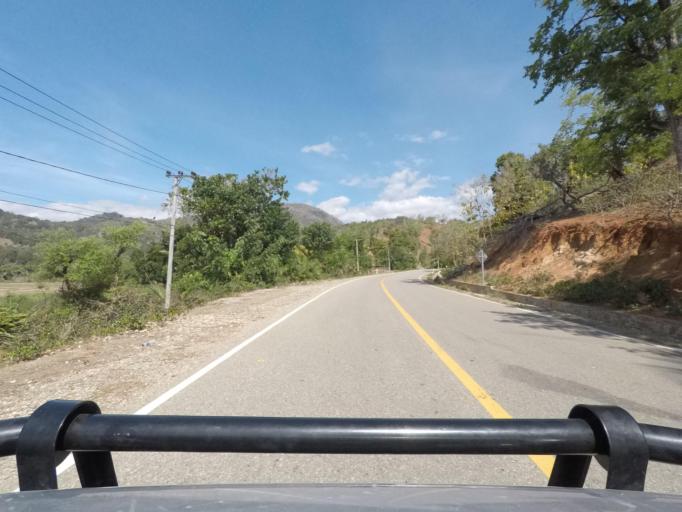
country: TL
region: Bobonaro
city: Maliana
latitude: -8.8718
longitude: 125.0418
